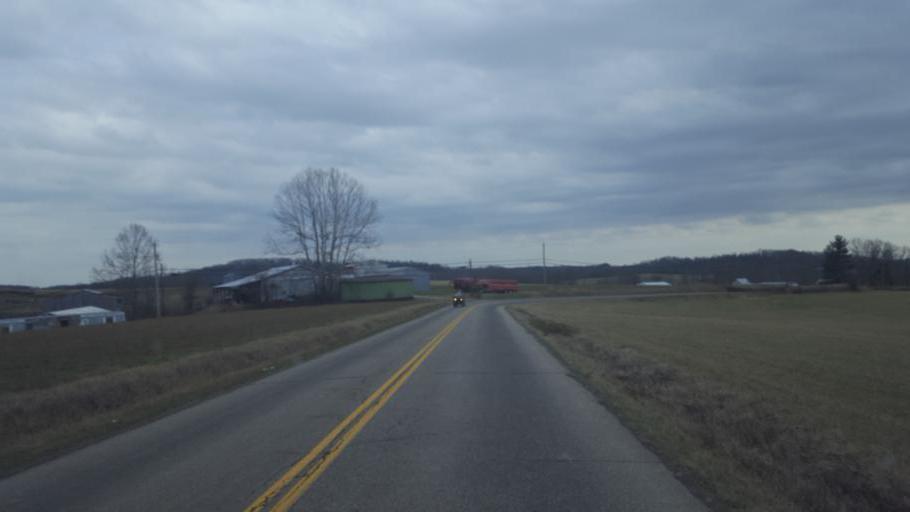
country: US
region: Ohio
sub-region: Gallia County
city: Gallipolis
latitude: 38.7926
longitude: -82.3984
